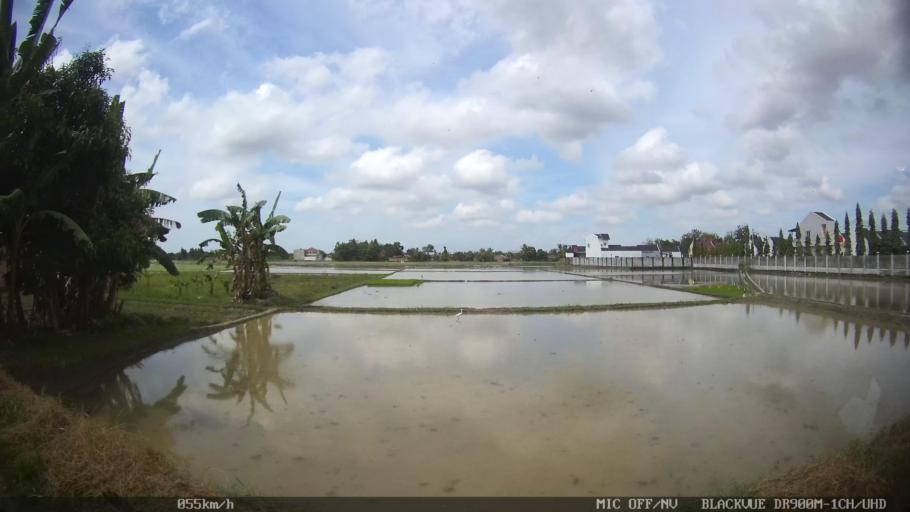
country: ID
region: North Sumatra
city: Percut
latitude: 3.5658
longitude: 98.8560
